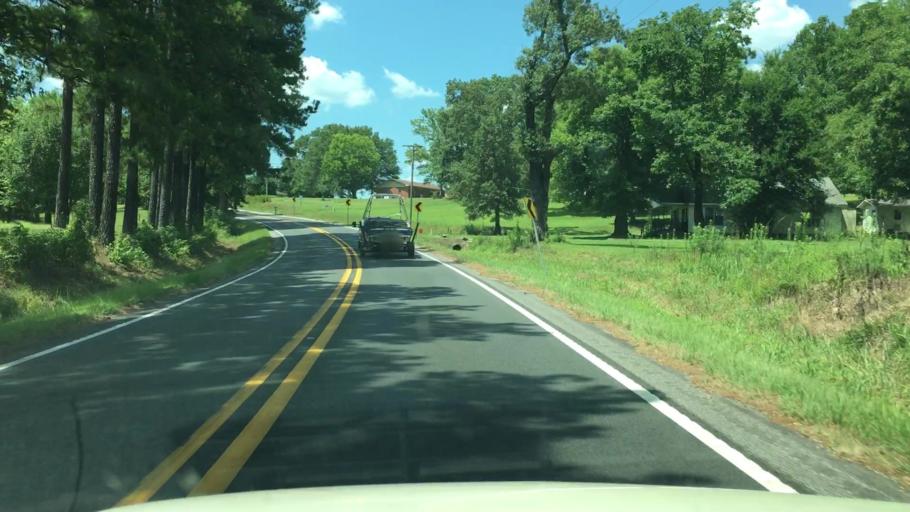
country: US
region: Arkansas
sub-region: Clark County
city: Arkadelphia
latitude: 34.2632
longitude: -93.1305
